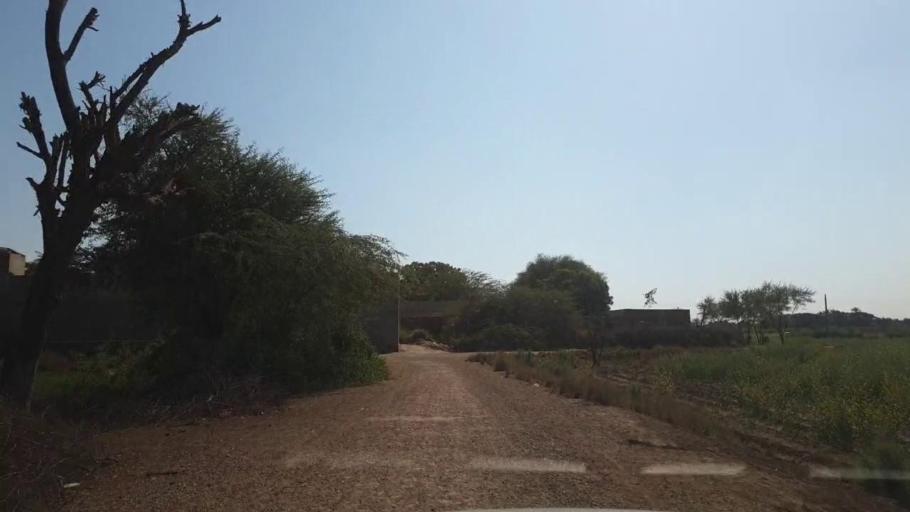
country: PK
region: Sindh
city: Tando Adam
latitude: 25.6397
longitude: 68.6883
